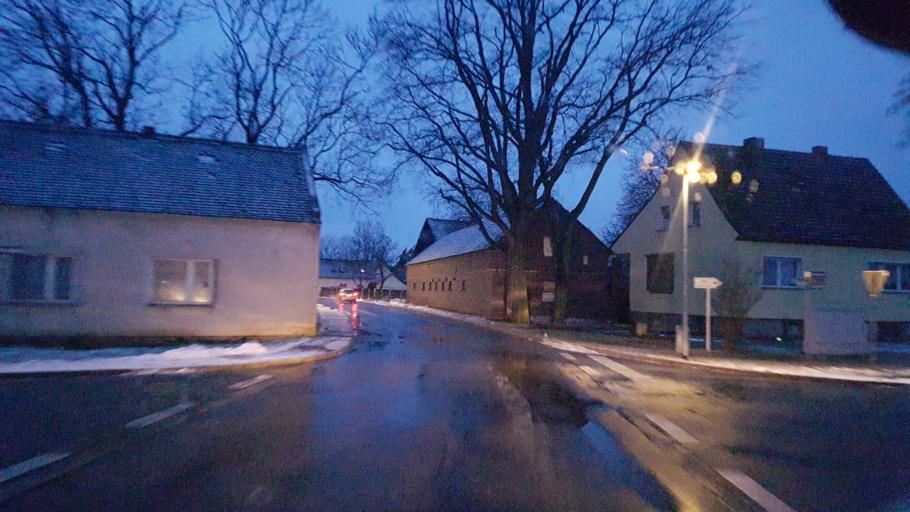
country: DE
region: Brandenburg
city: Werben
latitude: 51.7805
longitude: 14.2012
